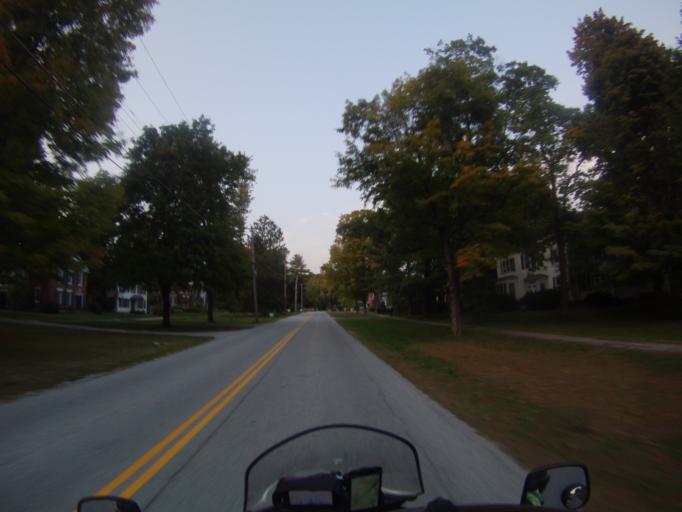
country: US
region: Vermont
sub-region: Rutland County
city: Brandon
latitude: 43.7981
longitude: -73.0942
